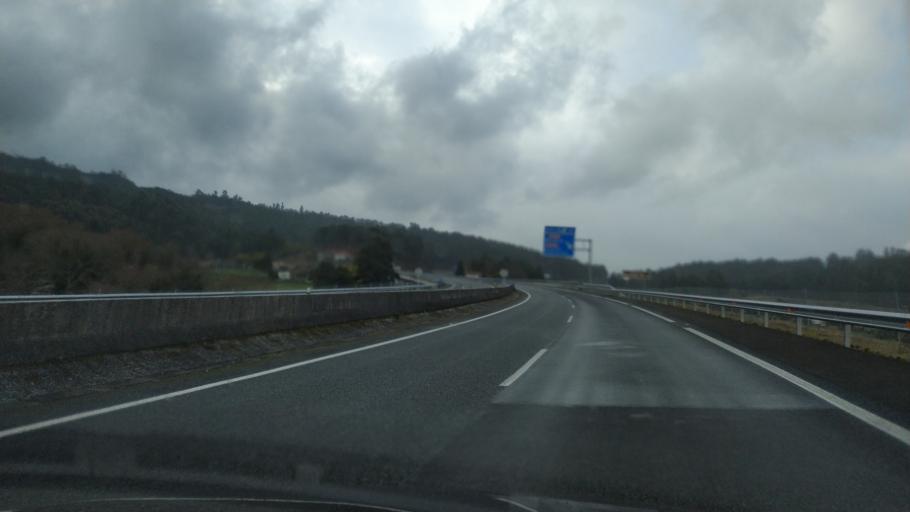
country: ES
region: Galicia
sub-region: Provincia de Pontevedra
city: Silleda
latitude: 42.7291
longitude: -8.3282
